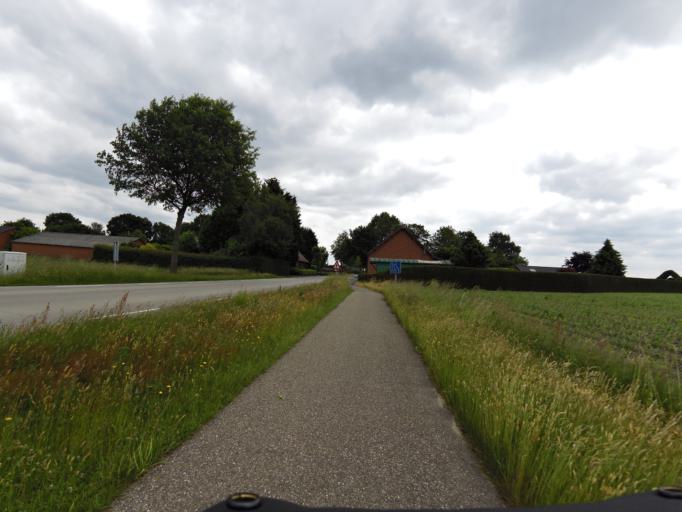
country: NL
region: North Brabant
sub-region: Gemeente Baarle-Nassau
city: Baarle-Nassau
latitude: 51.4470
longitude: 4.9080
